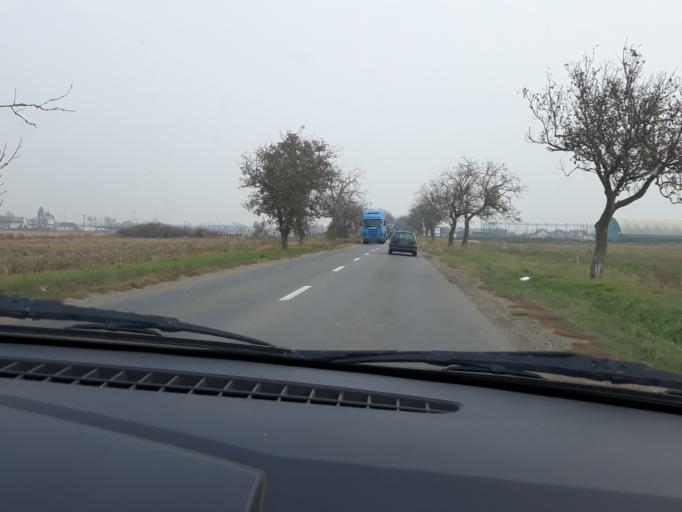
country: RO
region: Bihor
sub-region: Comuna Santandrei
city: Santandrei
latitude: 47.0534
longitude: 21.8725
